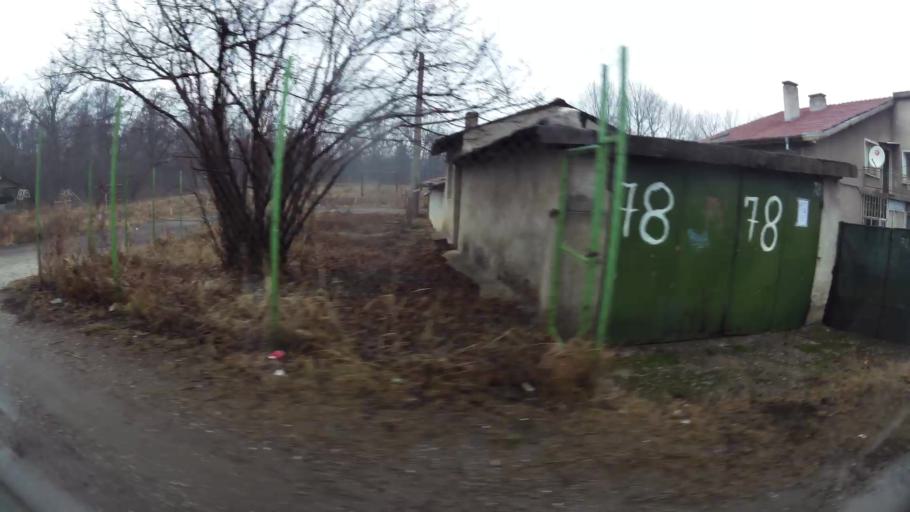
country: BG
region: Sofia-Capital
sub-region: Stolichna Obshtina
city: Sofia
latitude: 42.7081
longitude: 23.4249
